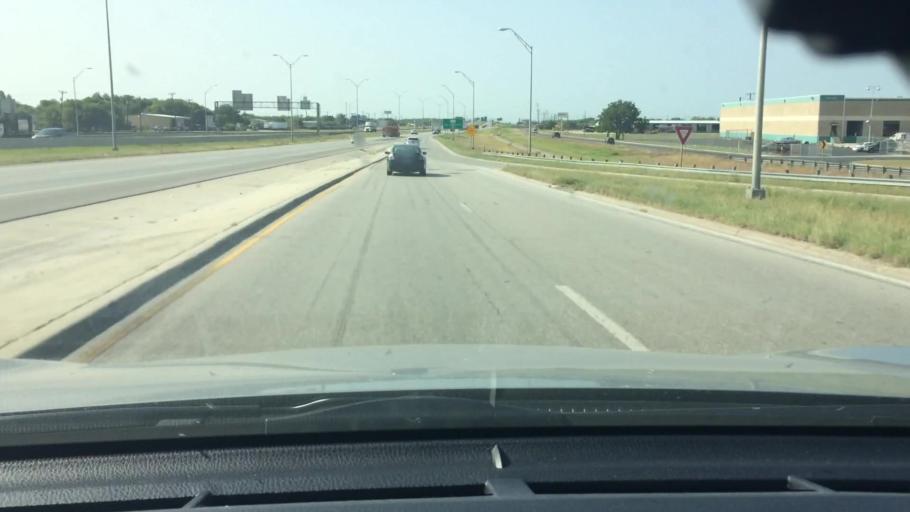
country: US
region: Texas
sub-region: Bexar County
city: Kirby
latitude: 29.4335
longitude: -98.3897
